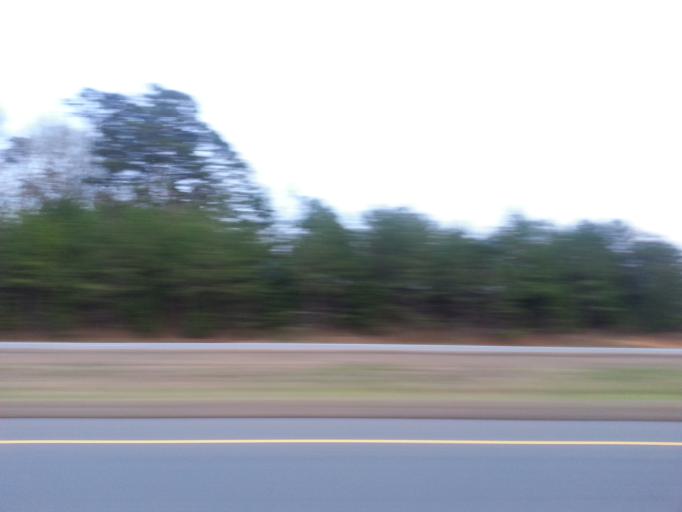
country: US
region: Tennessee
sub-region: McMinn County
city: Englewood
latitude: 35.3991
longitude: -84.4998
